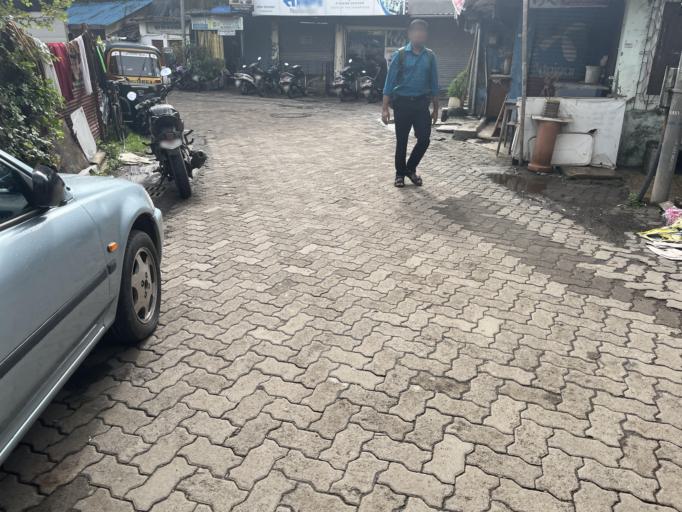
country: IN
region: Maharashtra
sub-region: Mumbai Suburban
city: Borivli
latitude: 19.2345
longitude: 72.8674
